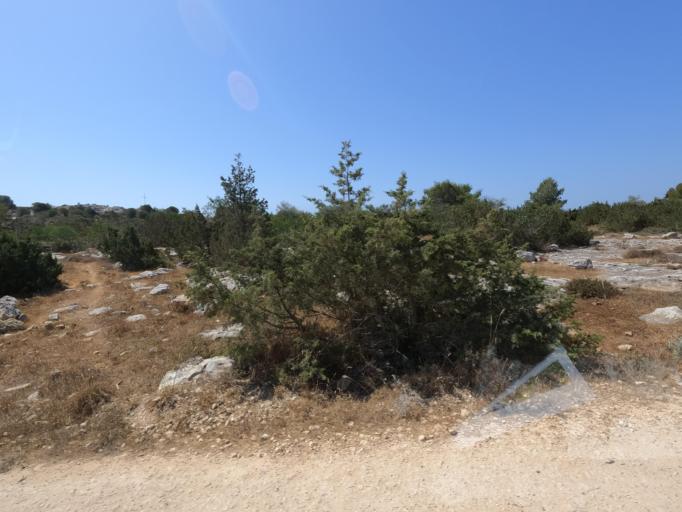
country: CY
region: Ammochostos
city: Paralimni
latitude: 35.0118
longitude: 33.9665
